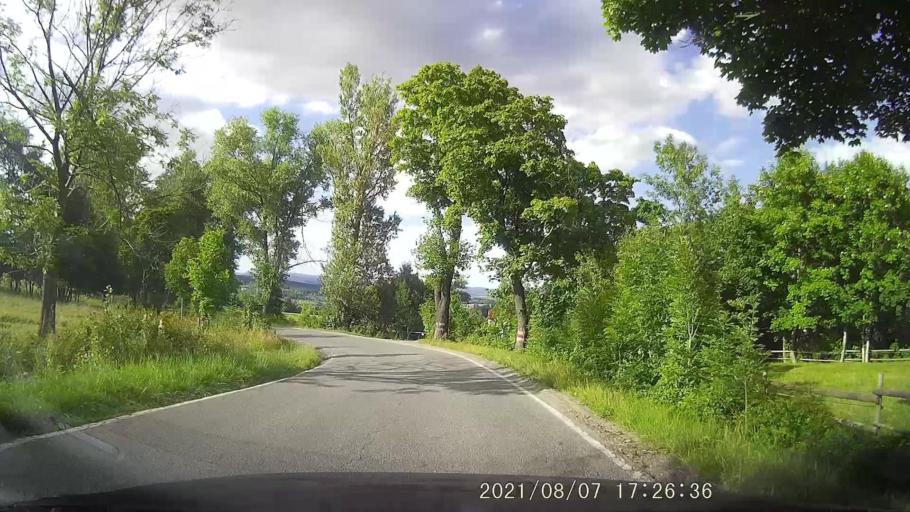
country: PL
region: Lower Silesian Voivodeship
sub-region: Powiat klodzki
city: Polanica-Zdroj
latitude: 50.3838
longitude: 16.5243
